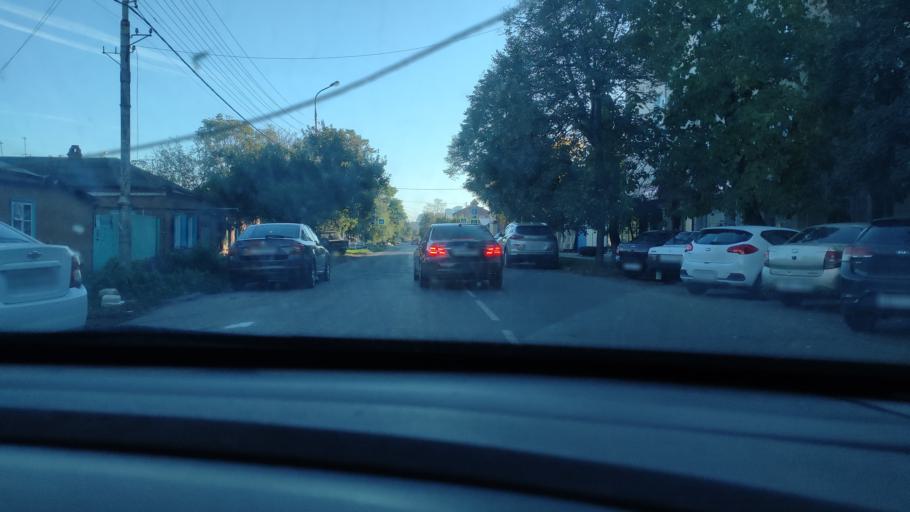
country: RU
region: Krasnodarskiy
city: Krasnodar
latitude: 45.0412
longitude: 38.9649
